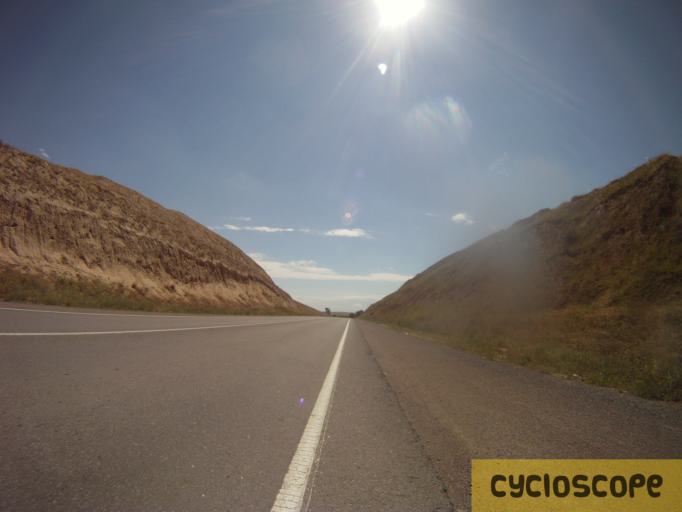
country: KG
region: Chuy
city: Bystrovka
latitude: 43.3300
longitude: 75.8935
